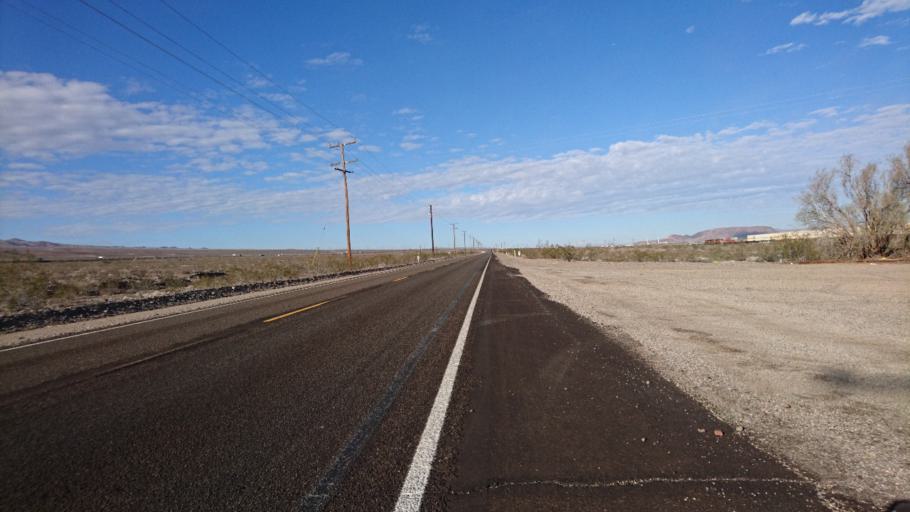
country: US
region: California
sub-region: San Bernardino County
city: Barstow
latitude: 34.8480
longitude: -116.7967
